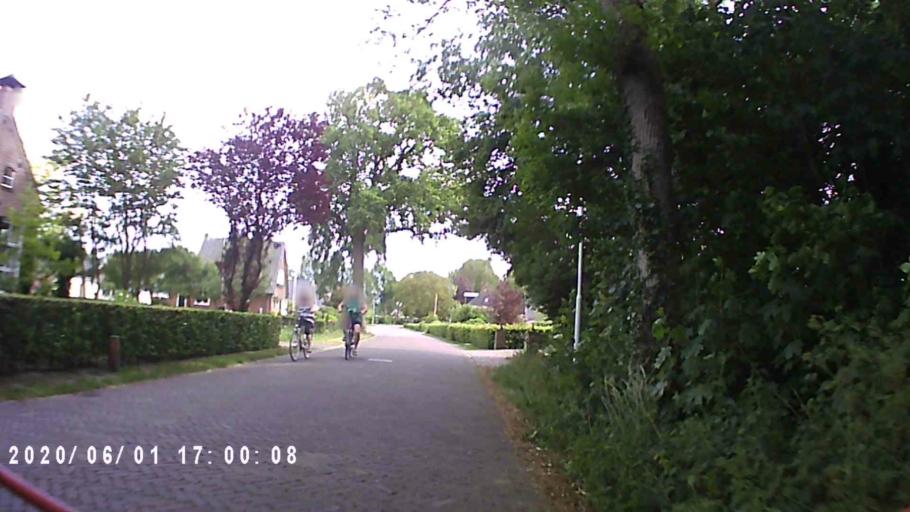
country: NL
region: Friesland
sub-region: Gemeente Tytsjerksteradiel
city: Hurdegaryp
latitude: 53.1839
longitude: 5.9291
